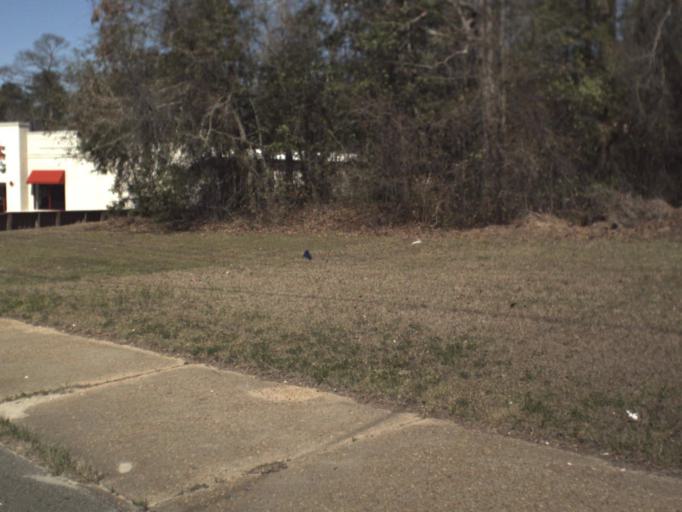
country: US
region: Florida
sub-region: Jackson County
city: Marianna
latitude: 30.7862
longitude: -85.2535
